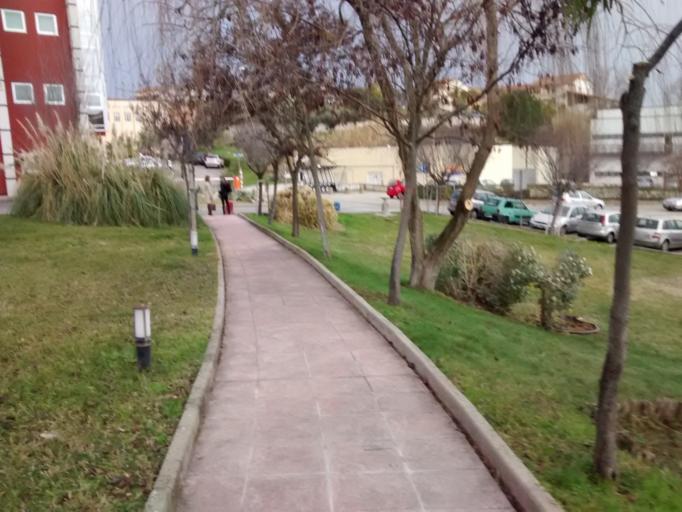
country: IT
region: Calabria
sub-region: Provincia di Cosenza
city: Quattromiglia
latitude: 39.3571
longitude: 16.2258
